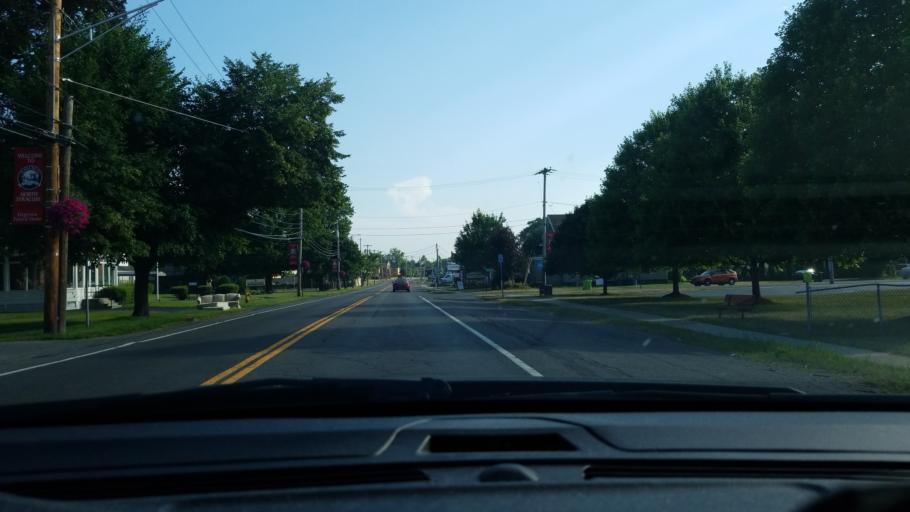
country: US
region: New York
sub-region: Onondaga County
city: North Syracuse
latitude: 43.1342
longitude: -76.1304
